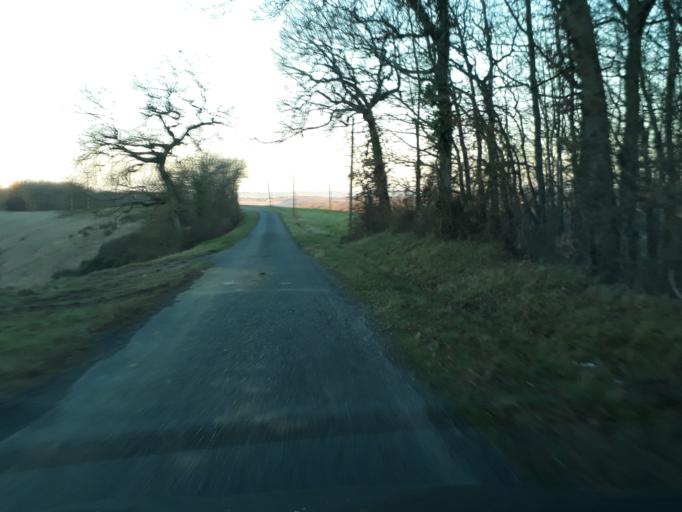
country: FR
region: Midi-Pyrenees
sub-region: Departement du Gers
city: Pavie
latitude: 43.6099
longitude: 0.6805
